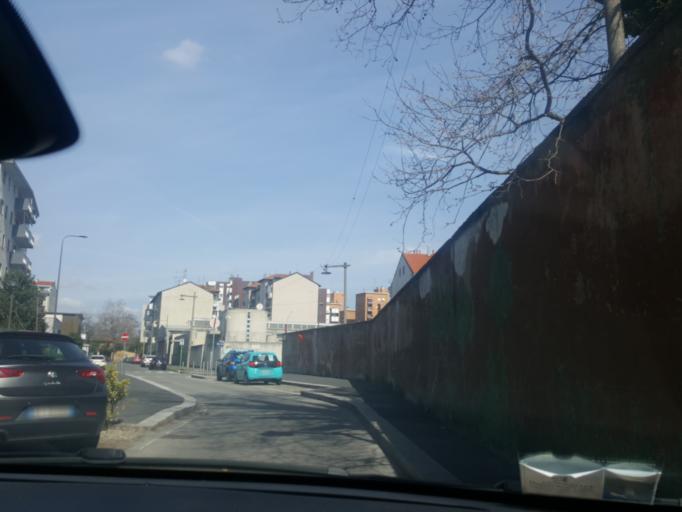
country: IT
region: Lombardy
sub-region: Citta metropolitana di Milano
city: Novate Milanese
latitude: 45.4992
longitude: 9.1361
